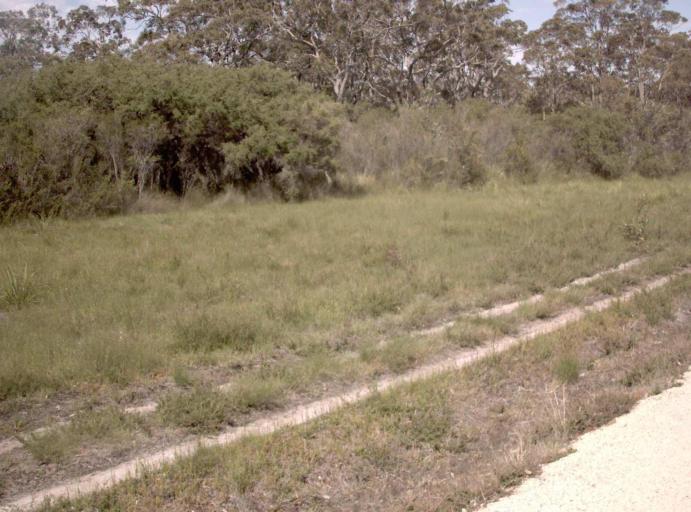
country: AU
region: New South Wales
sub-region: Bega Valley
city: Eden
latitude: -37.5480
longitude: 149.7260
